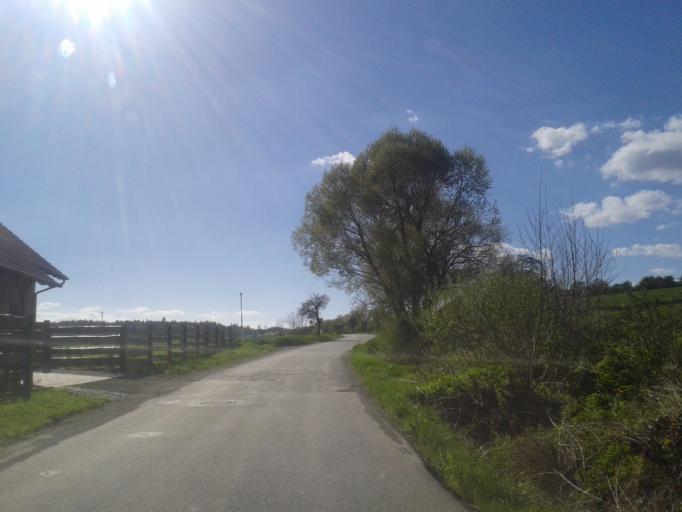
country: CZ
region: Central Bohemia
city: Hostomice
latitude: 49.8755
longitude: 14.0996
